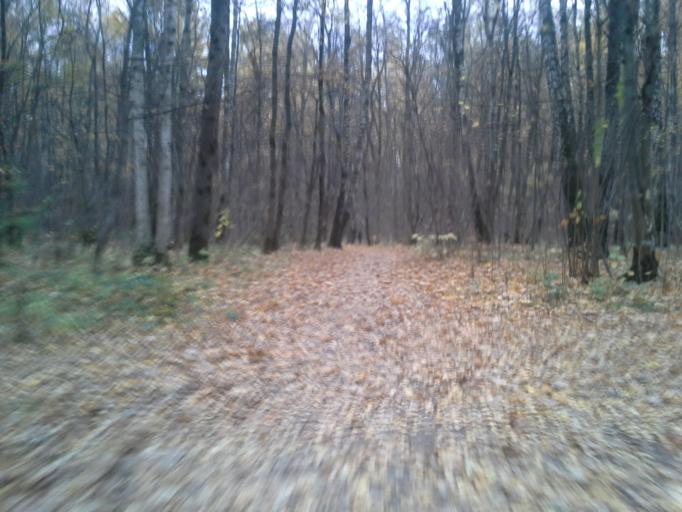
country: RU
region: Moscow
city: Chertanovo Yuzhnoye
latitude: 55.6133
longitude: 37.5725
